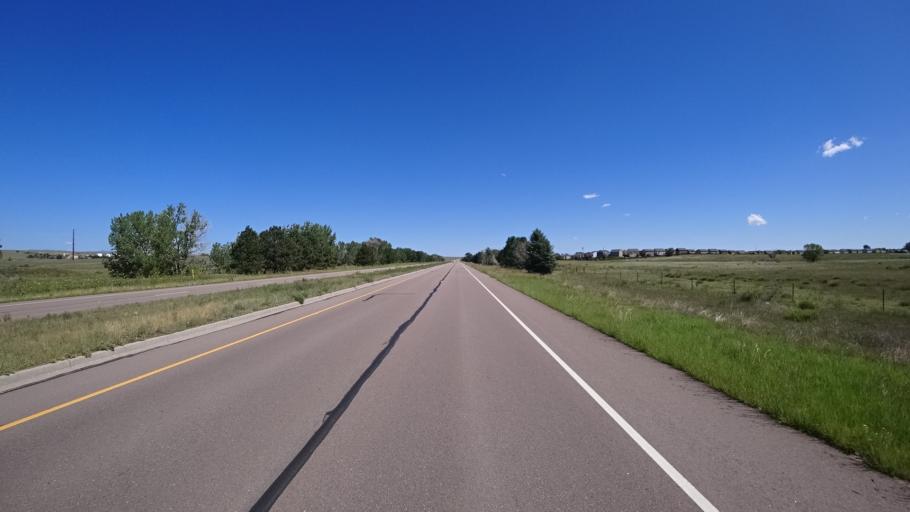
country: US
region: Colorado
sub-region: El Paso County
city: Security-Widefield
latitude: 38.7712
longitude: -104.6596
